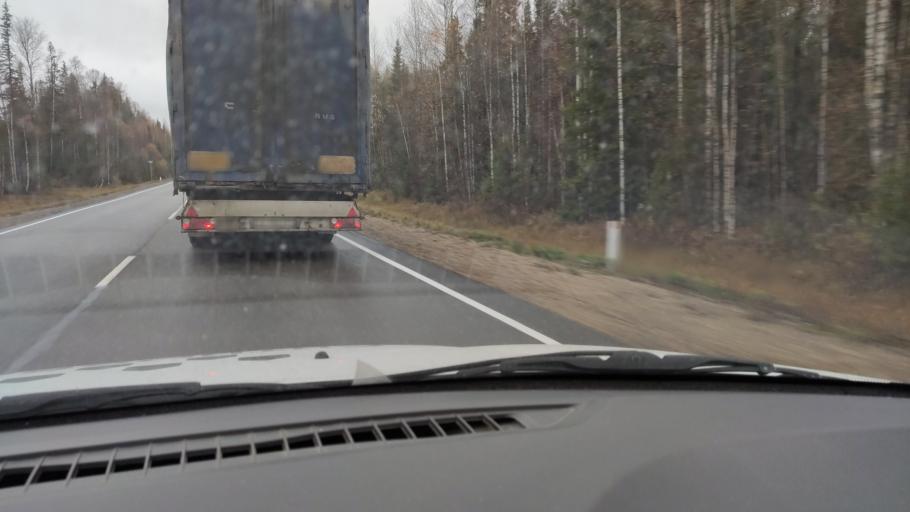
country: RU
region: Kirov
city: Chernaya Kholunitsa
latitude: 58.8363
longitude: 51.7550
